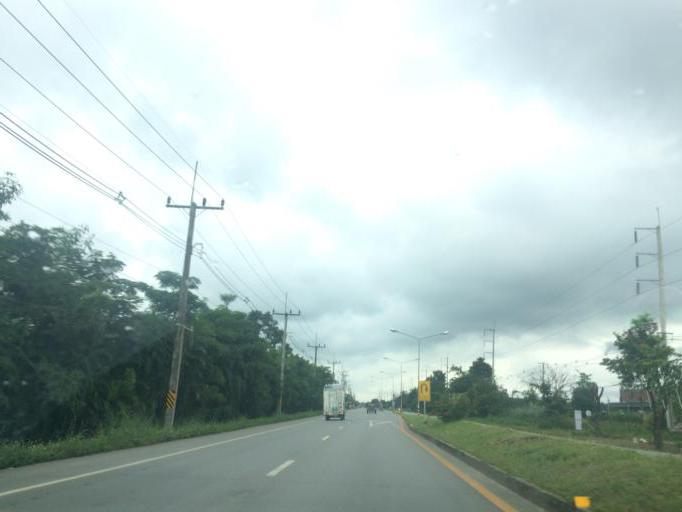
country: TH
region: Chiang Rai
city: Mae Chan
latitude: 20.0625
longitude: 99.8760
